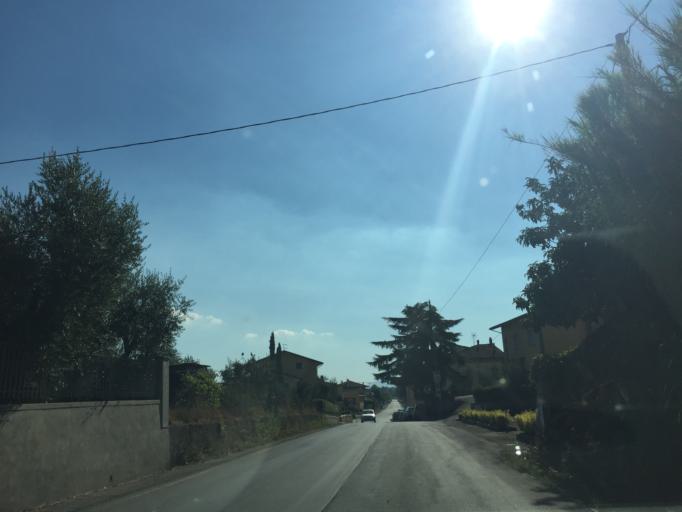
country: IT
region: Tuscany
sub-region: Provincia di Pistoia
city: San Rocco
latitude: 43.8171
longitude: 10.8591
